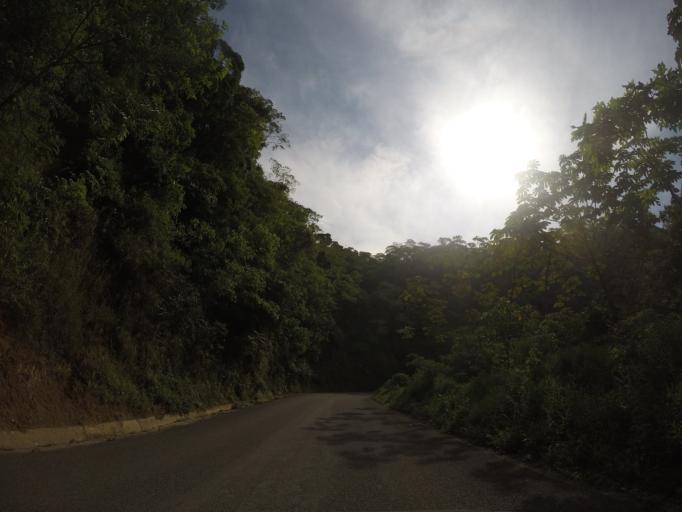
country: MX
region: Oaxaca
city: Pluma Hidalgo
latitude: 15.9336
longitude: -96.4294
